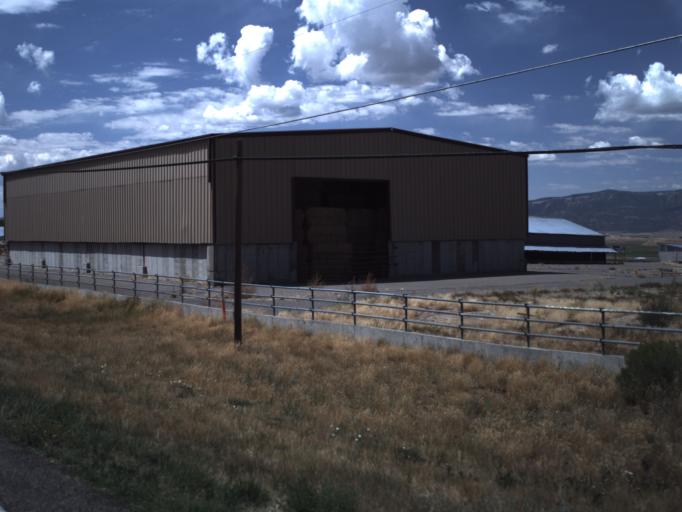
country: US
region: Utah
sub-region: Sanpete County
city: Mount Pleasant
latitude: 39.5230
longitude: -111.4716
